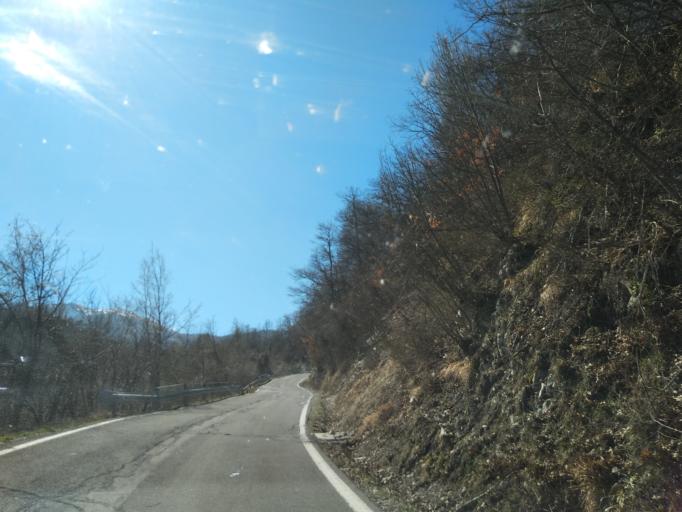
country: IT
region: Emilia-Romagna
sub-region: Provincia di Reggio Emilia
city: Ramiseto
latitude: 44.4085
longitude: 10.2719
